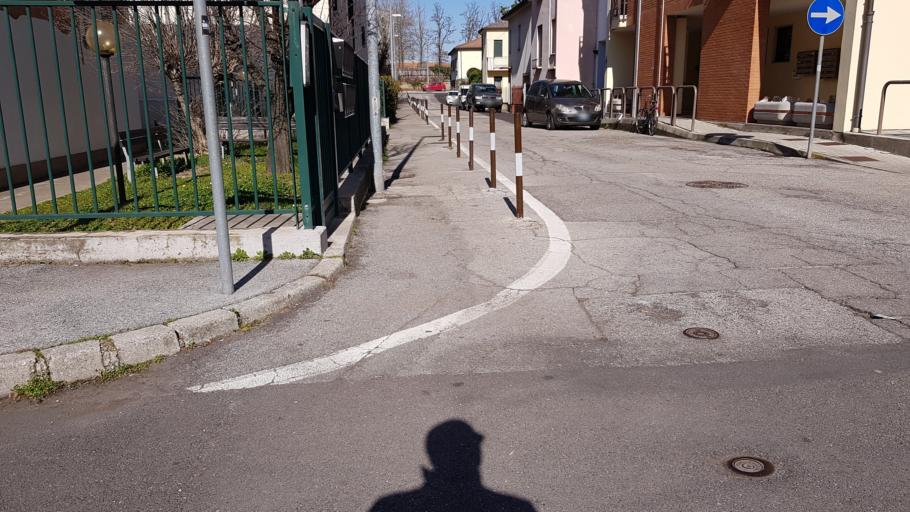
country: IT
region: Veneto
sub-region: Provincia di Padova
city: Padova
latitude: 45.4081
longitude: 11.8963
